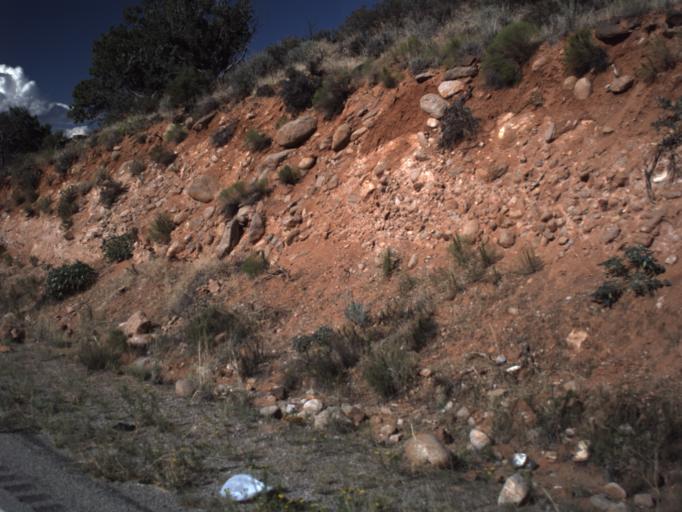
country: US
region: Utah
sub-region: Washington County
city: Toquerville
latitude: 37.2782
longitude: -113.3039
